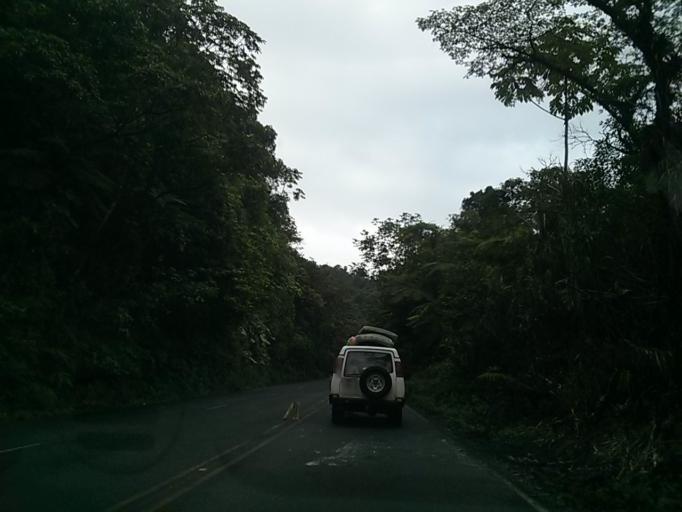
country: CR
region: San Jose
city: Dulce Nombre de Jesus
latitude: 10.1451
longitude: -83.9741
